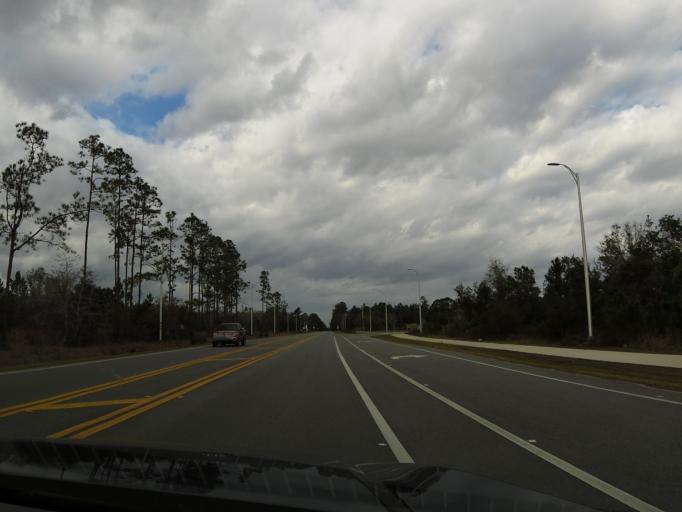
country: US
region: Florida
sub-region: Volusia County
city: Pierson
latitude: 29.2564
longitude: -81.4695
